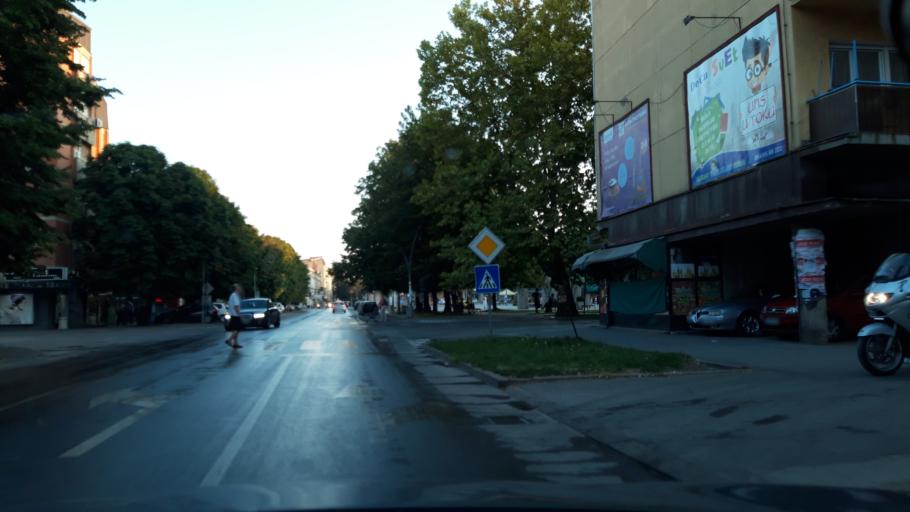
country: RS
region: Autonomna Pokrajina Vojvodina
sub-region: Sremski Okrug
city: Ruma
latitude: 45.0094
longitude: 19.8227
